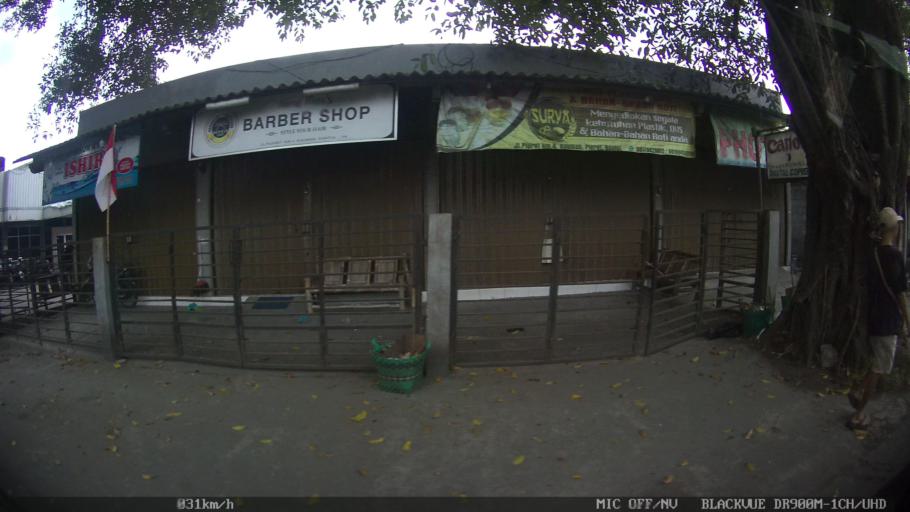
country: ID
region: Daerah Istimewa Yogyakarta
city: Sewon
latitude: -7.8650
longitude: 110.4080
